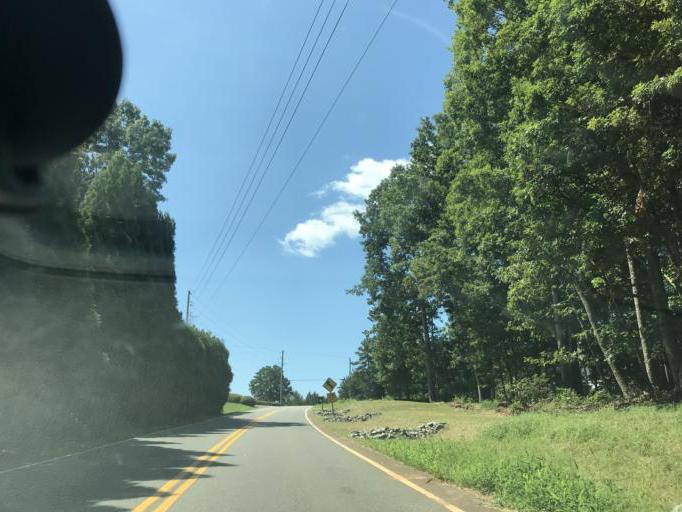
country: US
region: Georgia
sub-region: Dawson County
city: Dawsonville
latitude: 34.3062
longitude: -84.0287
